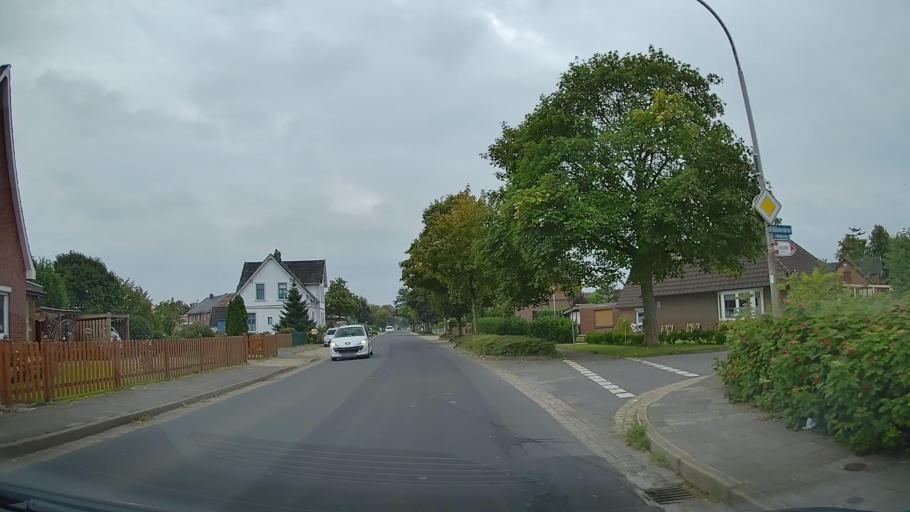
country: DE
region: Lower Saxony
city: Freiburg
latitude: 53.8231
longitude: 9.2885
